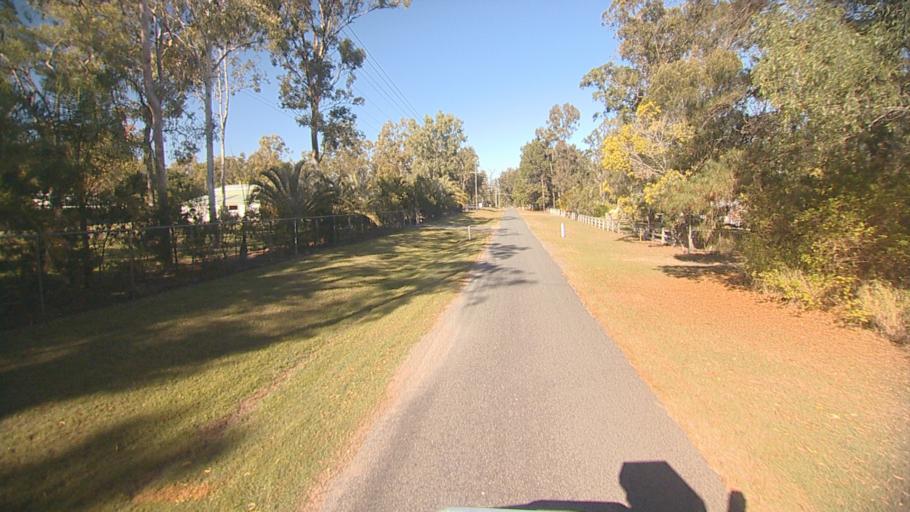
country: AU
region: Queensland
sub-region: Logan
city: Park Ridge South
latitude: -27.7534
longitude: 153.0470
